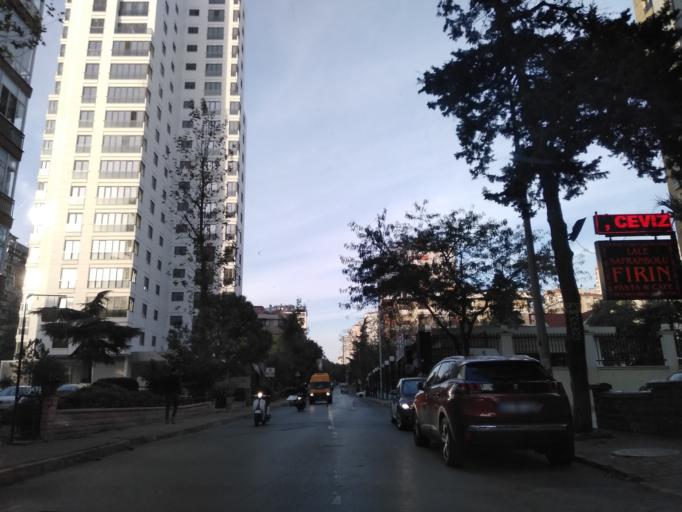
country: TR
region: Istanbul
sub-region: Atasehir
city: Atasehir
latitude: 40.9690
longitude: 29.0890
